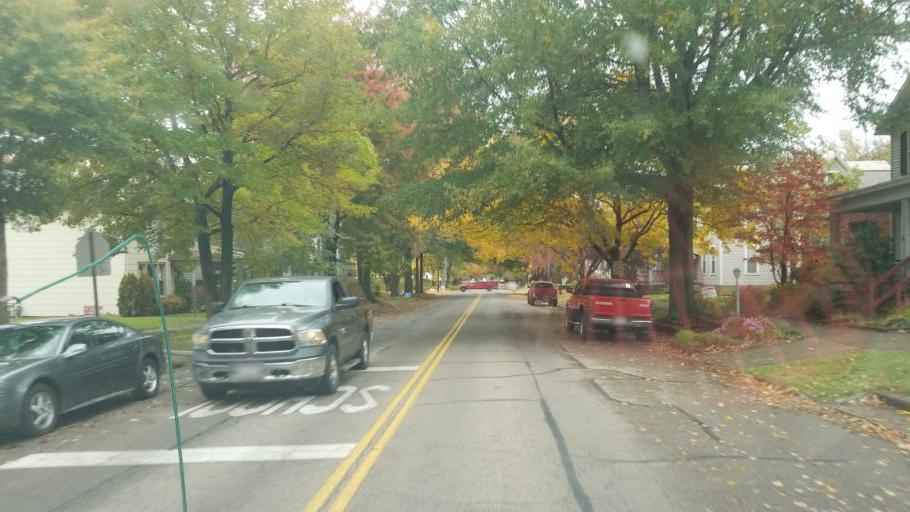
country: US
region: Ohio
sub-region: Washington County
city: Marietta
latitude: 39.4242
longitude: -81.4593
